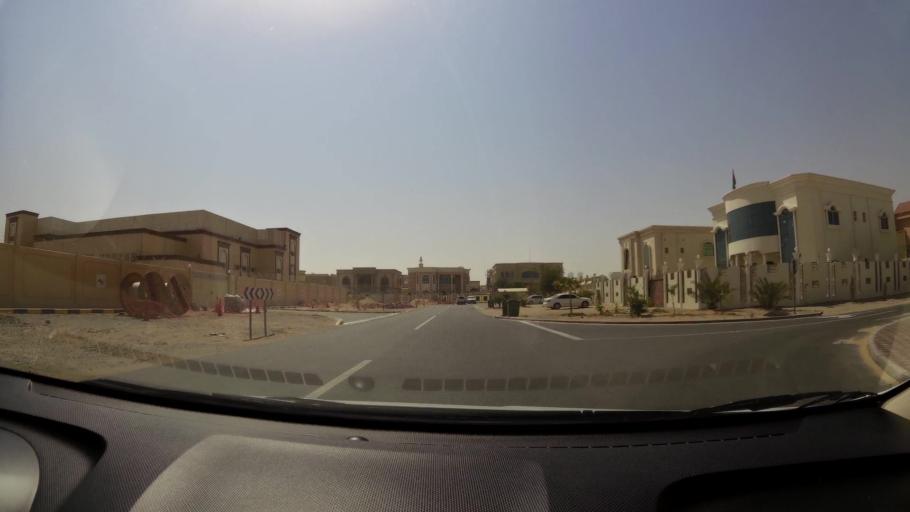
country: AE
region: Ajman
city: Ajman
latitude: 25.4074
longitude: 55.5478
